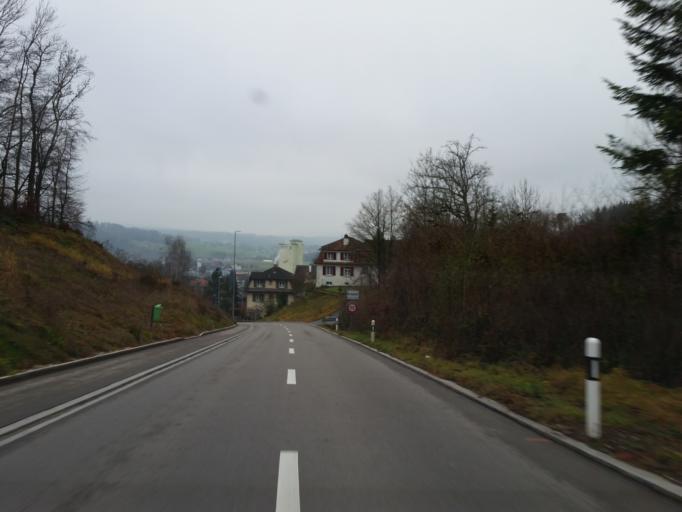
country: CH
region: Thurgau
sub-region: Weinfelden District
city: Sulgen
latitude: 47.5277
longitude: 9.2073
